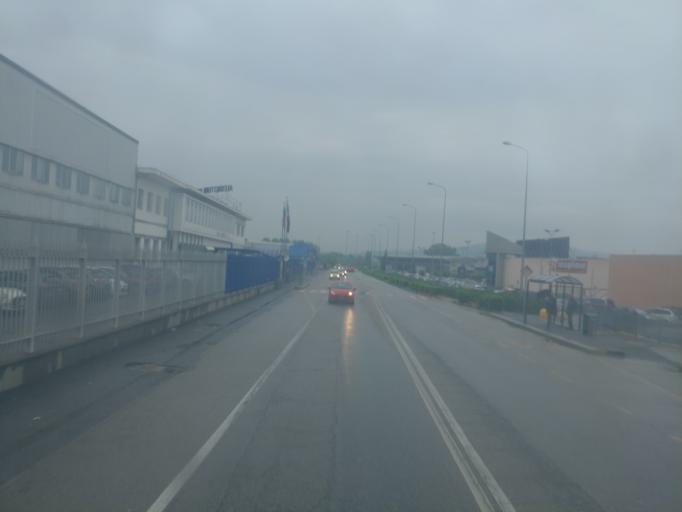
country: IT
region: Piedmont
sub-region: Provincia di Torino
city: La Loggia
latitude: 44.9628
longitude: 7.6684
